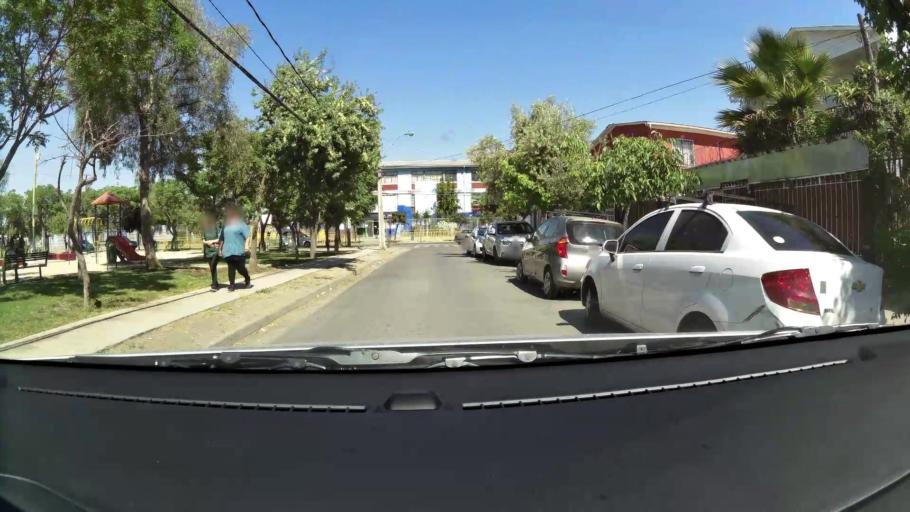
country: CL
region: Santiago Metropolitan
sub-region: Provincia de Santiago
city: La Pintana
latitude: -33.5599
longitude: -70.6575
